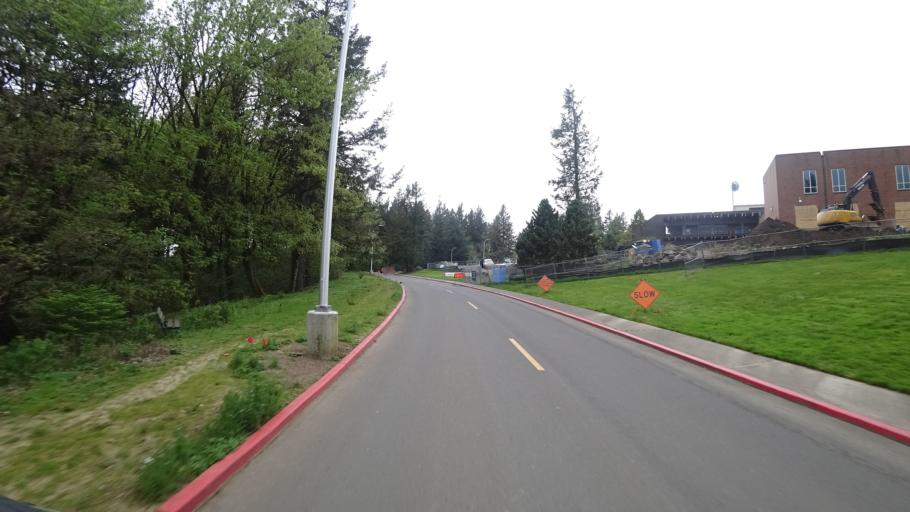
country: US
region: Oregon
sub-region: Washington County
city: Metzger
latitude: 45.4360
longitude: -122.7314
